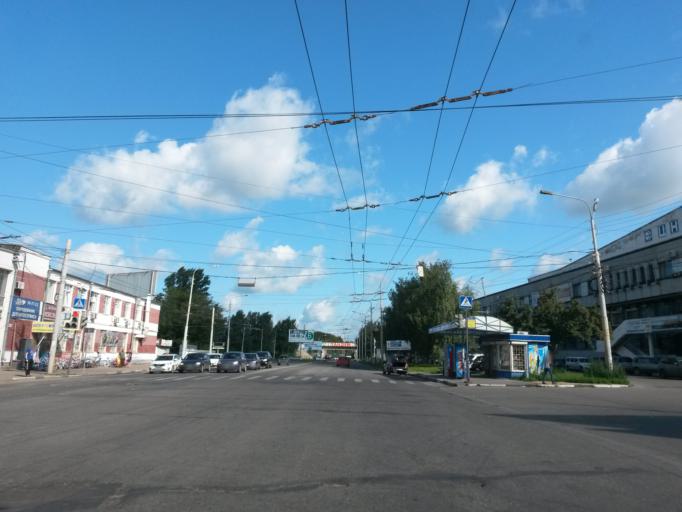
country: RU
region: Jaroslavl
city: Yaroslavl
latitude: 57.6433
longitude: 39.8826
